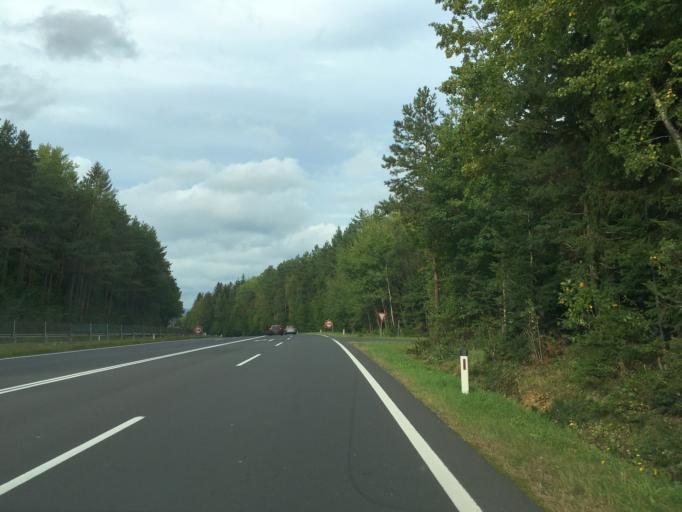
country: AT
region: Styria
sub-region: Politischer Bezirk Hartberg-Fuerstenfeld
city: Grafendorf bei Hartberg
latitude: 47.3519
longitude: 16.0110
